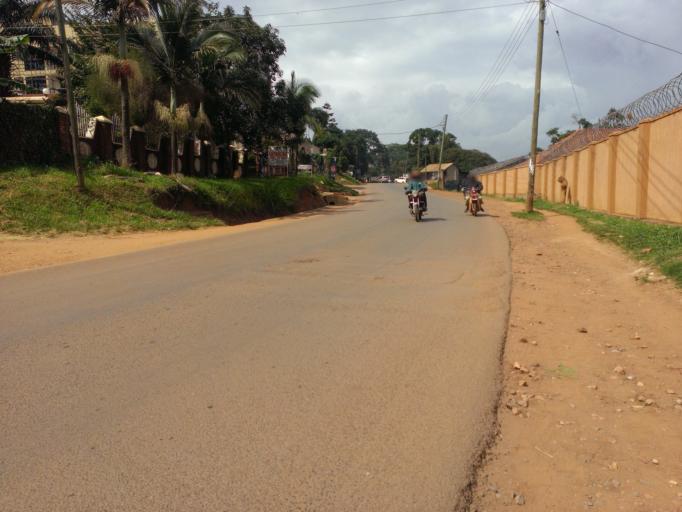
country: UG
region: Central Region
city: Kampala Central Division
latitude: 0.3195
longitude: 32.5576
